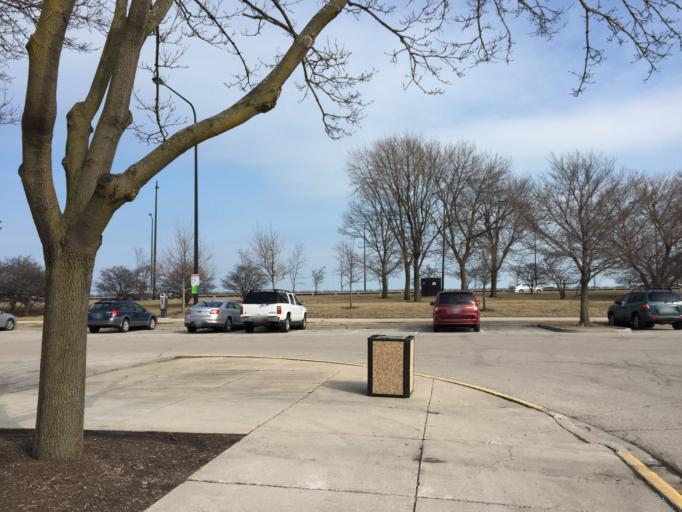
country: US
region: Illinois
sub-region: Cook County
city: Chicago
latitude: 41.7909
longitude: -87.5807
